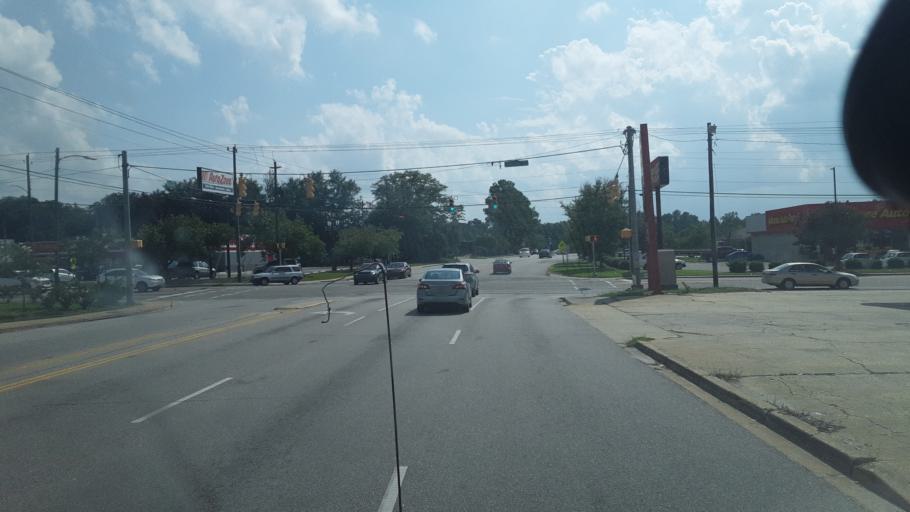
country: US
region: South Carolina
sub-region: Sumter County
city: Sumter
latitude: 33.9383
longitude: -80.3606
